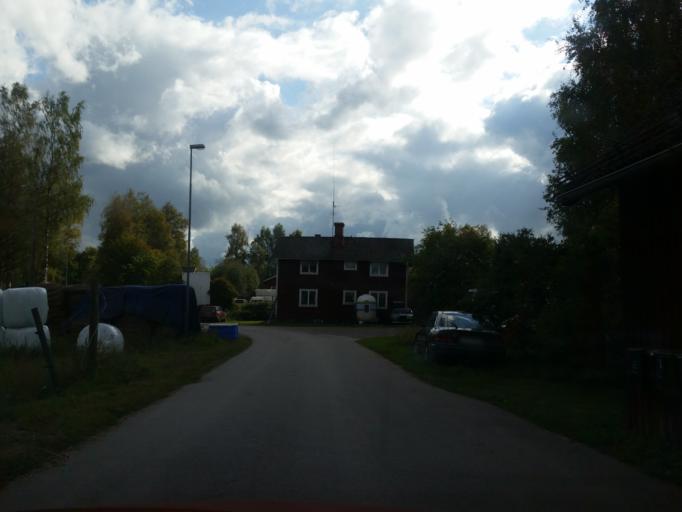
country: SE
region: Dalarna
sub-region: Leksand Municipality
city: Smedby
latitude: 60.6714
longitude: 15.1269
